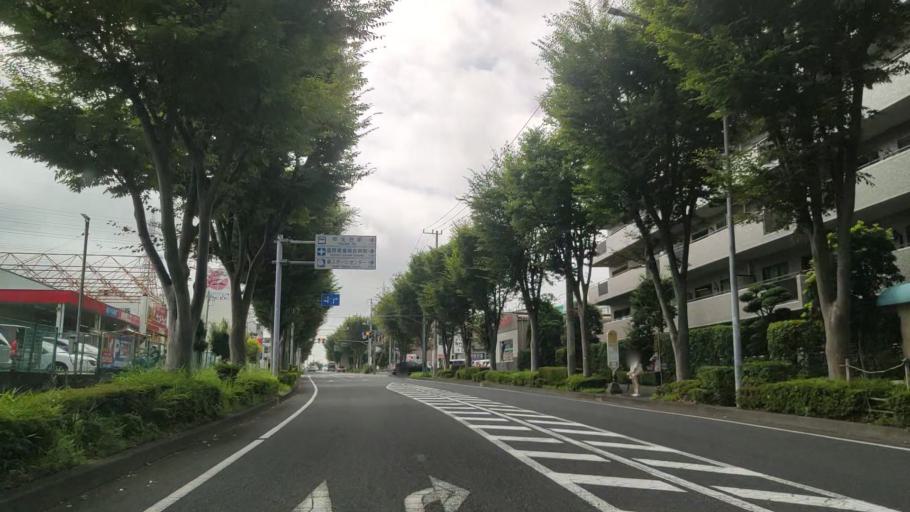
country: JP
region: Kanagawa
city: Fujisawa
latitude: 35.4188
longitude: 139.5233
